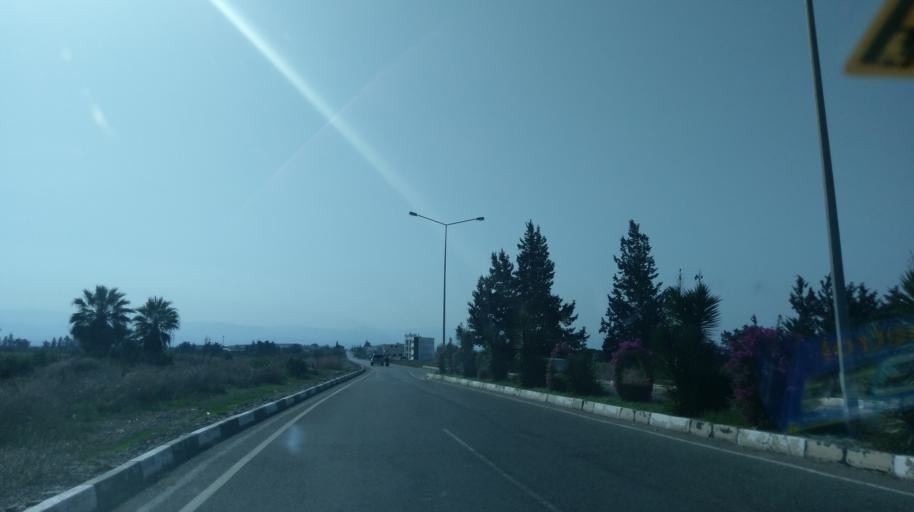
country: CY
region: Lefkosia
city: Morfou
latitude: 35.2405
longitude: 33.0263
